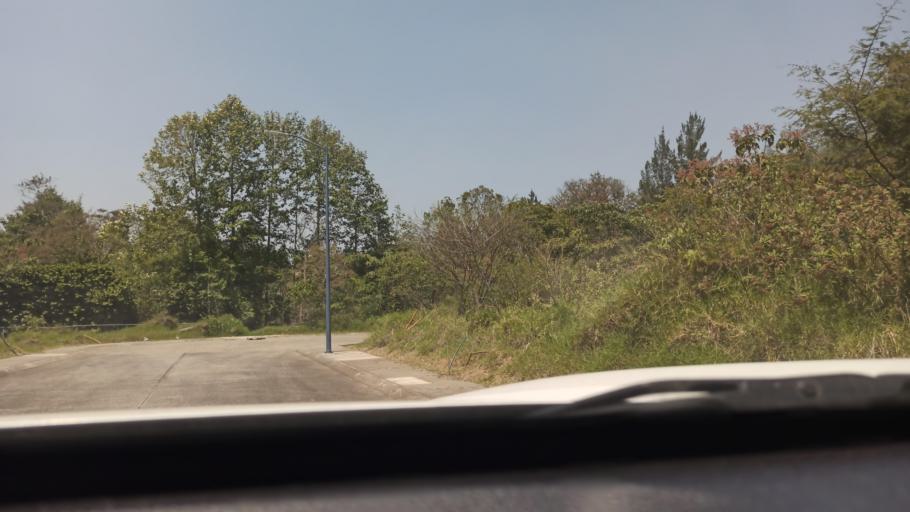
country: MX
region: Veracruz
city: El Castillo
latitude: 19.5263
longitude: -96.8745
